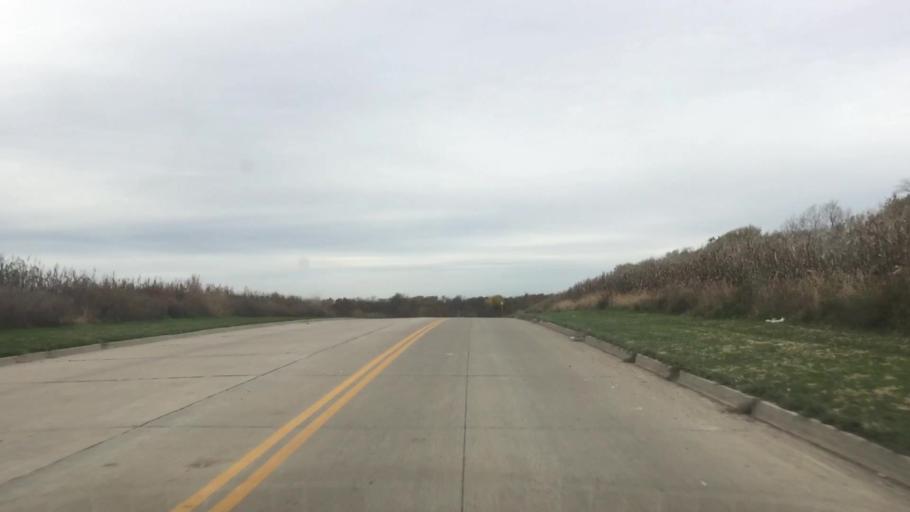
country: US
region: Missouri
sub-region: Jackson County
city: Greenwood
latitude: 38.8792
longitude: -94.3589
